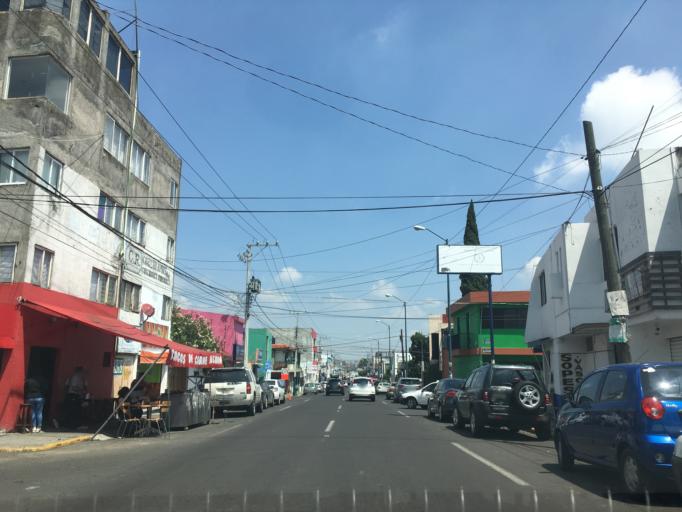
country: MX
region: Michoacan
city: Morelia
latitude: 19.6840
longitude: -101.1907
